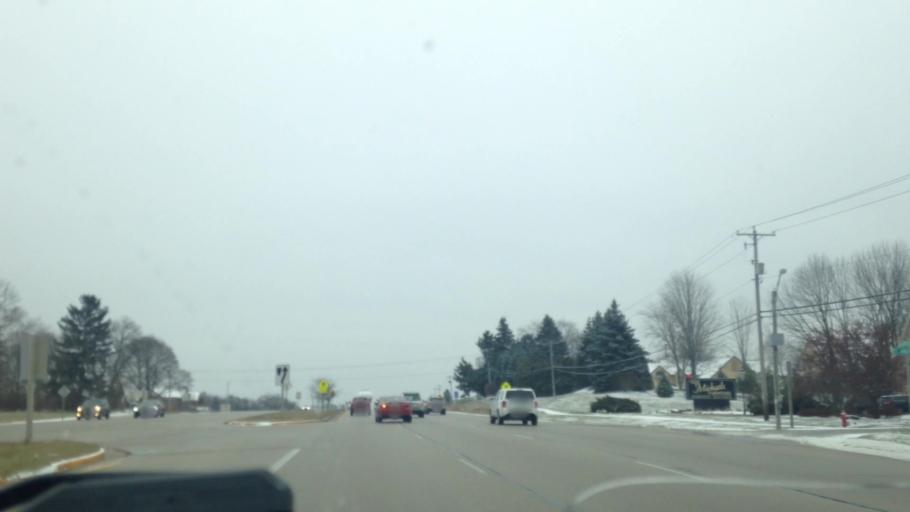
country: US
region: Wisconsin
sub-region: Waukesha County
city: Brookfield
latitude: 43.0905
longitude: -88.1435
